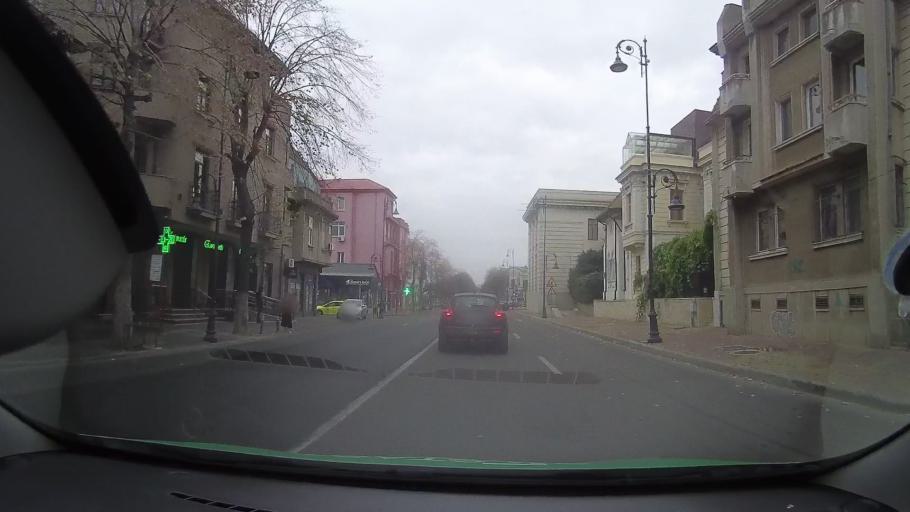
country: RO
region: Constanta
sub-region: Municipiul Constanta
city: Constanta
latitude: 44.1790
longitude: 28.6526
